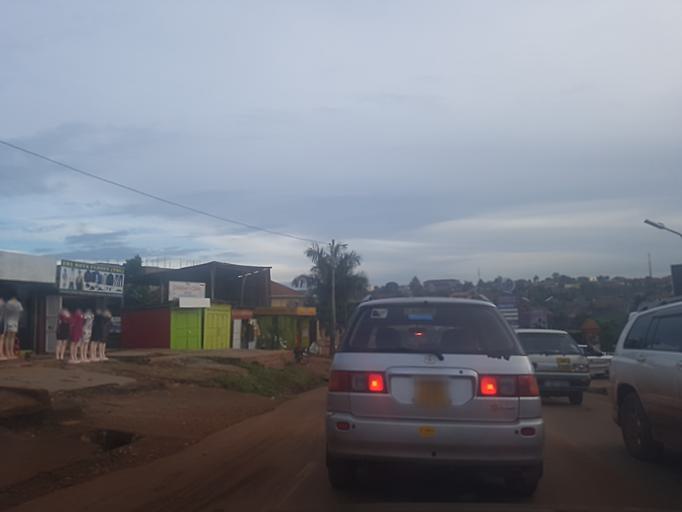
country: UG
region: Central Region
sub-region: Wakiso District
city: Kireka
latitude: 0.3756
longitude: 32.6439
